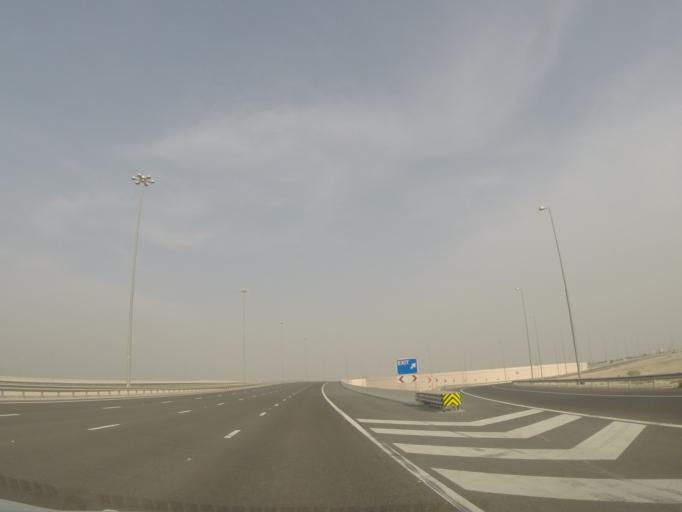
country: AE
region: Abu Dhabi
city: Abu Dhabi
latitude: 24.6967
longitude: 54.7746
